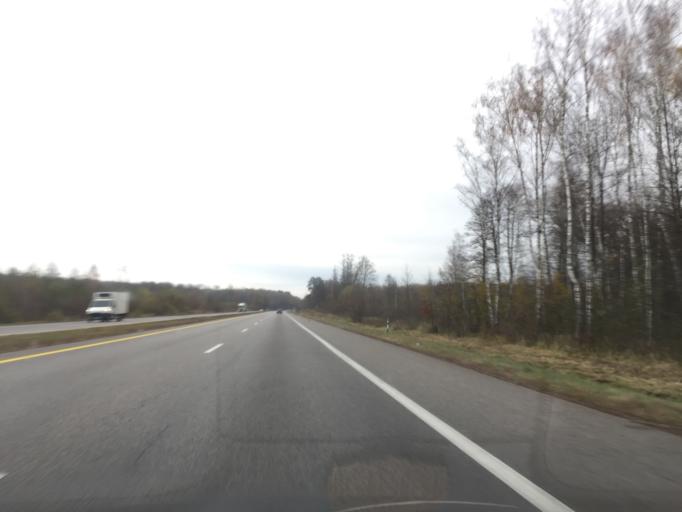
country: BY
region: Gomel
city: Gomel
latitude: 52.3682
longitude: 30.7498
